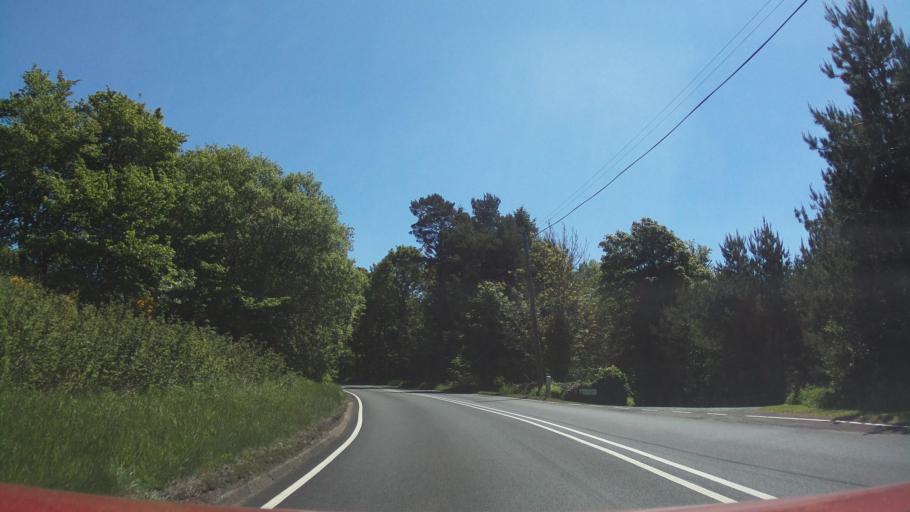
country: GB
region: Scotland
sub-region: Fife
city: Pathhead
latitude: 55.7352
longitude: -2.9010
